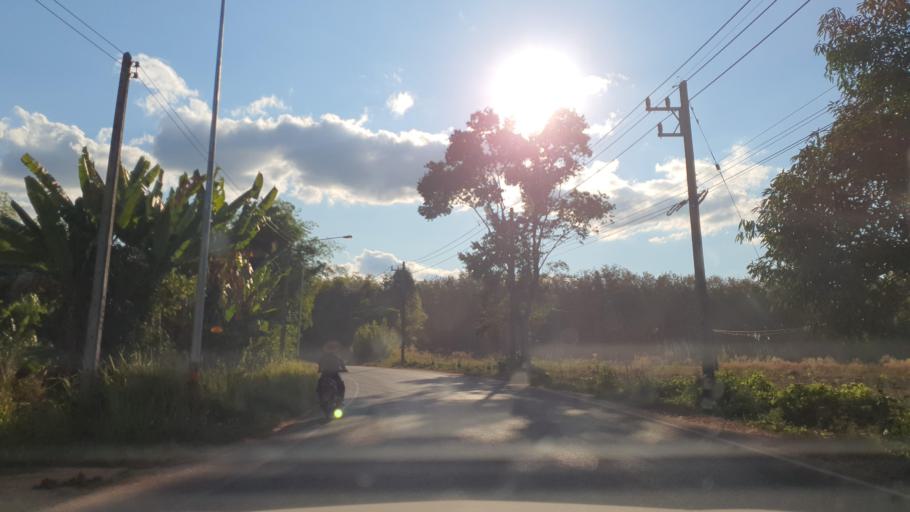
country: TH
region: Changwat Bueng Kan
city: Si Wilai
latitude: 18.1485
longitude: 103.8984
